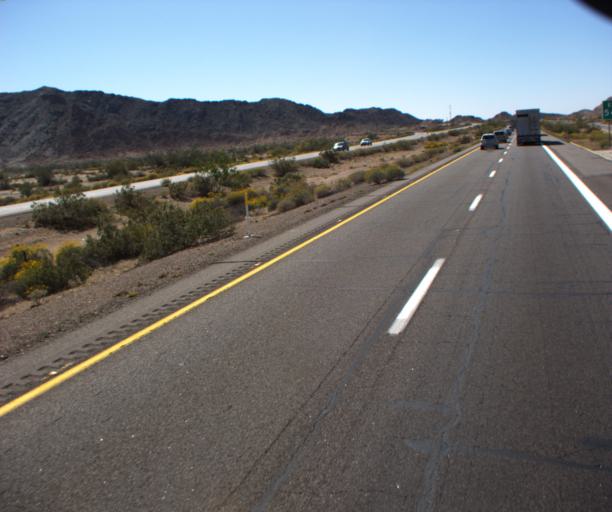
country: US
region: Arizona
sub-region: Yuma County
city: Wellton
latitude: 32.7300
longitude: -113.7274
